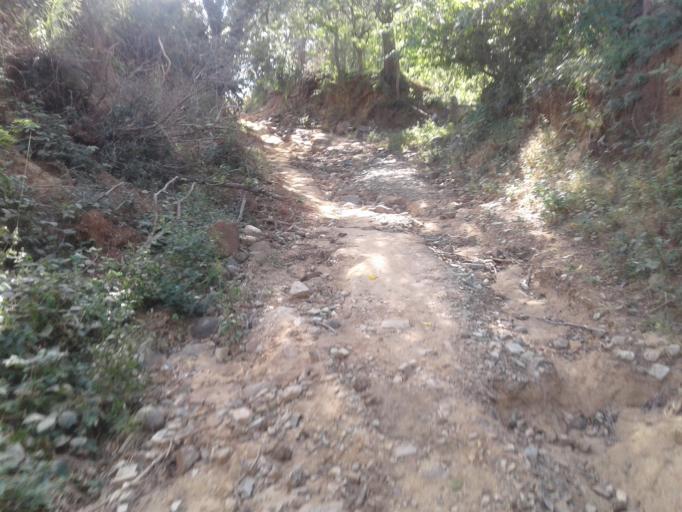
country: NI
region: Carazo
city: Santa Teresa
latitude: 11.6290
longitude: -86.1919
